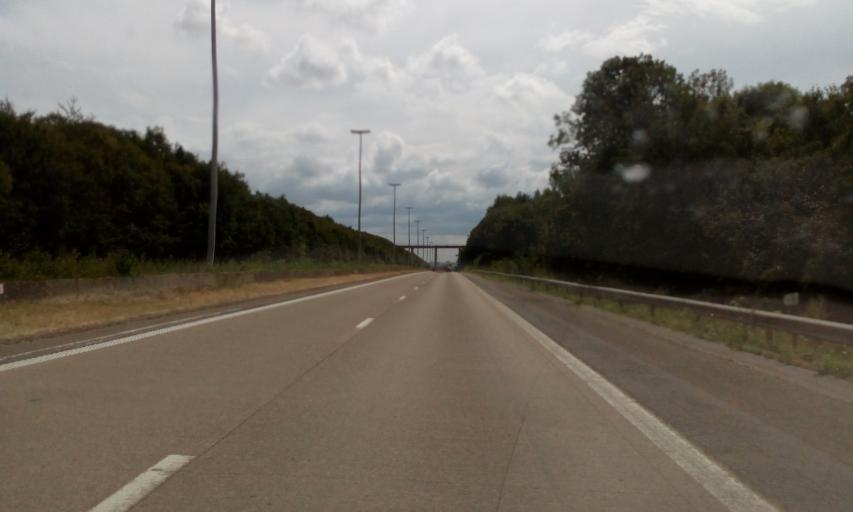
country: BE
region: Wallonia
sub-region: Province de Namur
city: Assesse
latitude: 50.3487
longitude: 5.0092
